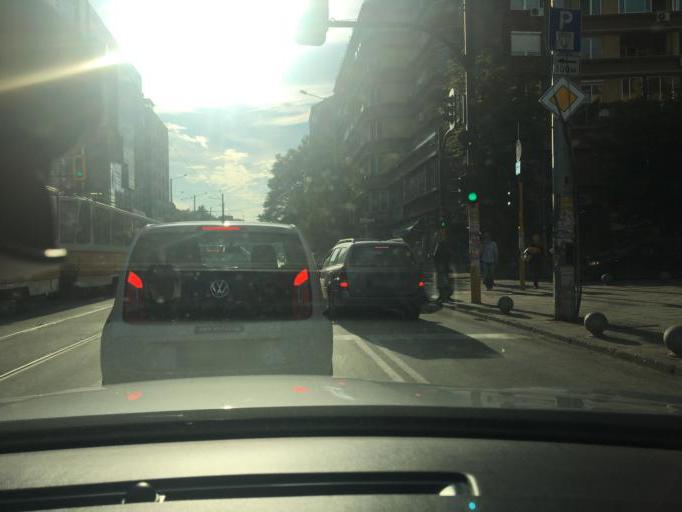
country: BG
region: Sofia-Capital
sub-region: Stolichna Obshtina
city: Sofia
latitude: 42.6793
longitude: 23.3614
